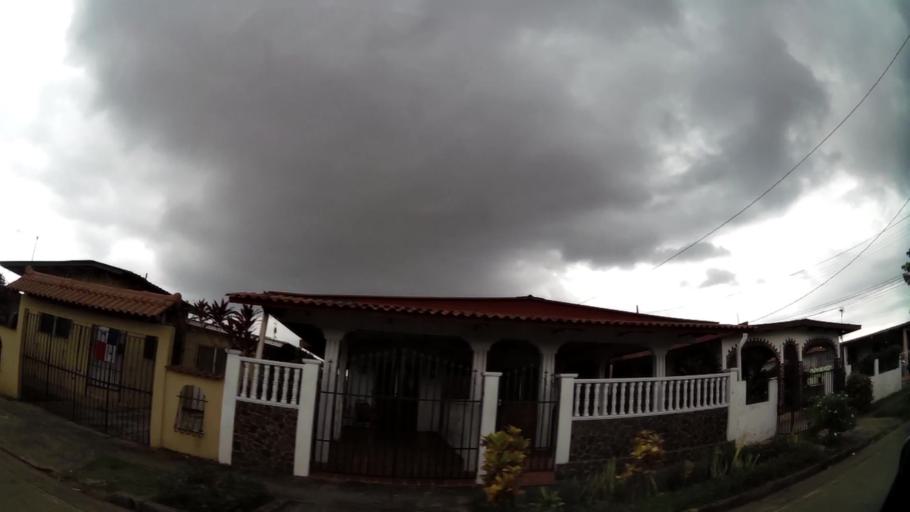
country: PA
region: Panama
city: Tocumen
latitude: 9.0574
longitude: -79.4166
